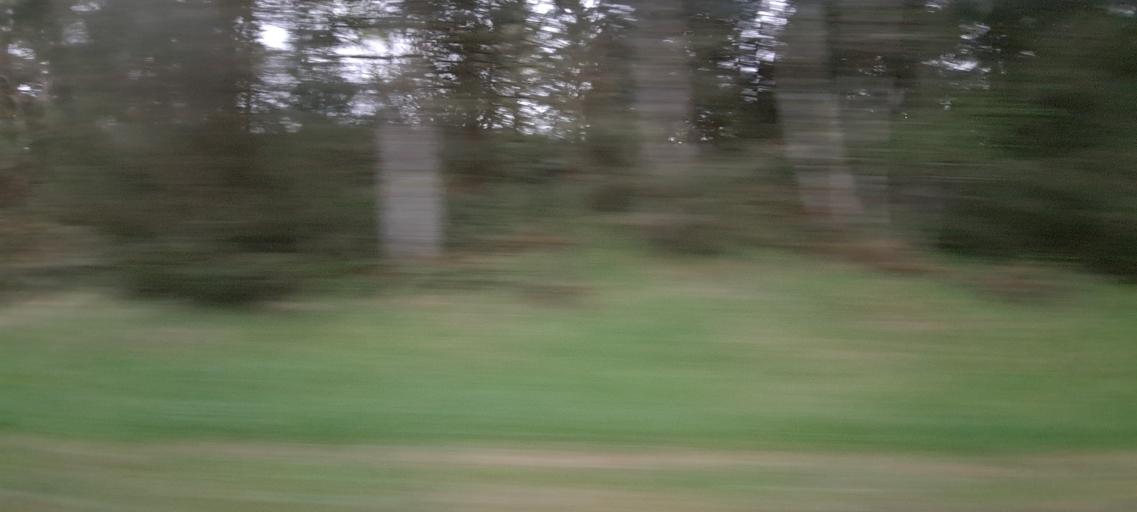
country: US
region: Oregon
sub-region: Clatsop County
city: Warrenton
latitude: 46.1606
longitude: -123.9474
